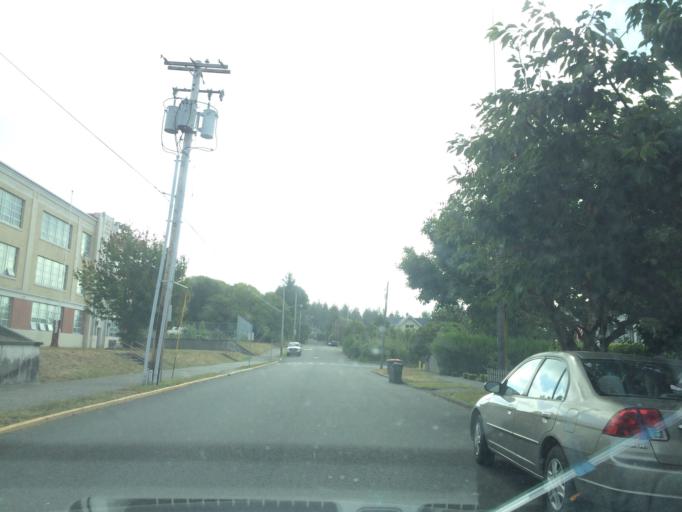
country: US
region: Oregon
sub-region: Clatsop County
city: Astoria
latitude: 46.1814
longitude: -123.8532
